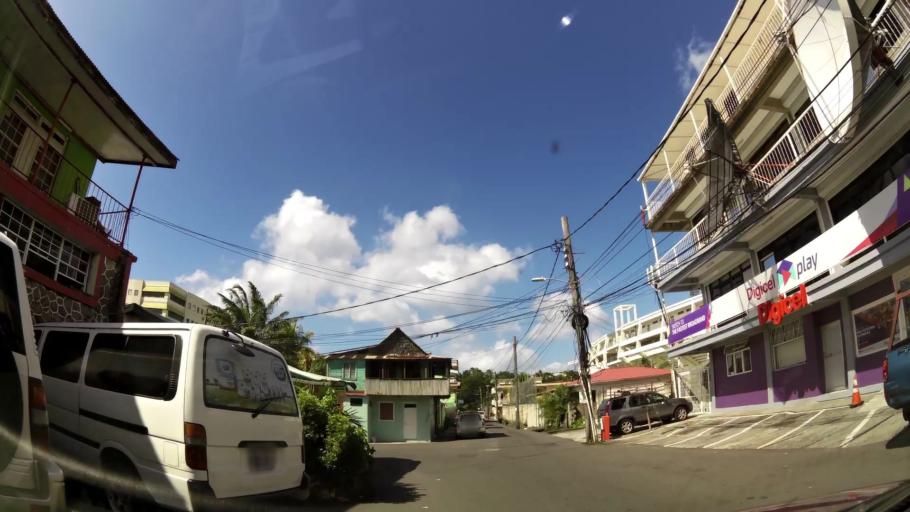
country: DM
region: Saint George
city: Roseau
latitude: 15.3004
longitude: -61.3848
